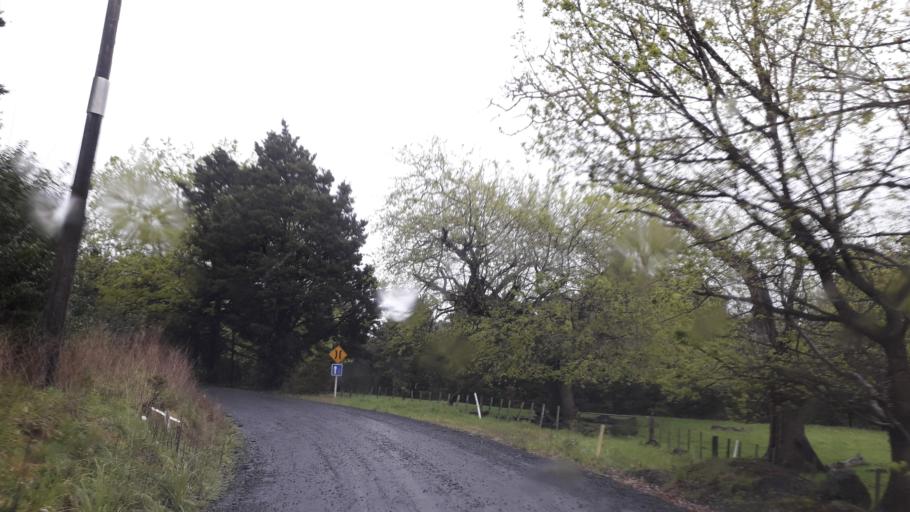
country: NZ
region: Northland
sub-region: Far North District
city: Waimate North
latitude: -35.4705
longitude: 173.6821
